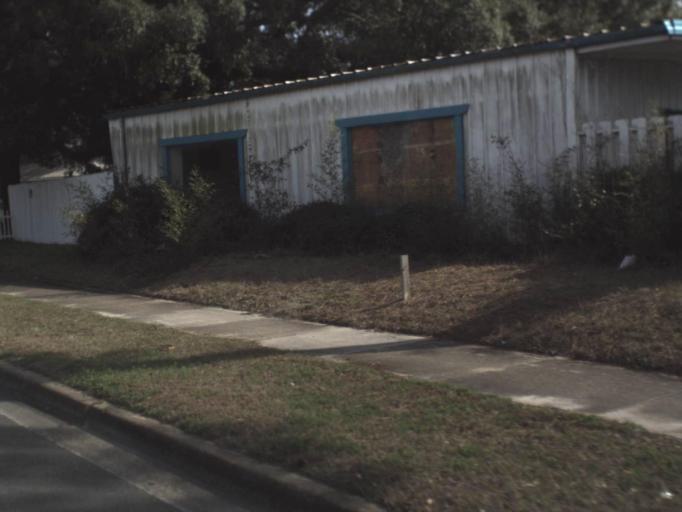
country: US
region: Florida
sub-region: Bay County
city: Pretty Bayou
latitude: 30.1803
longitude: -85.7043
